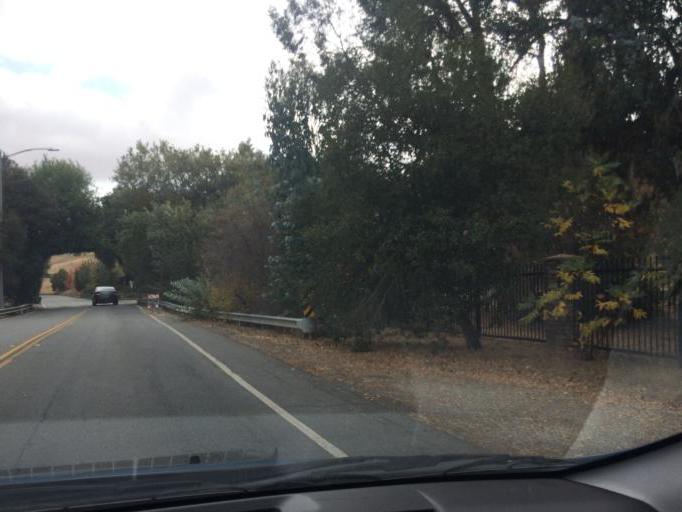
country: US
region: California
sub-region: Santa Clara County
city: Seven Trees
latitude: 37.2865
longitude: -121.7634
